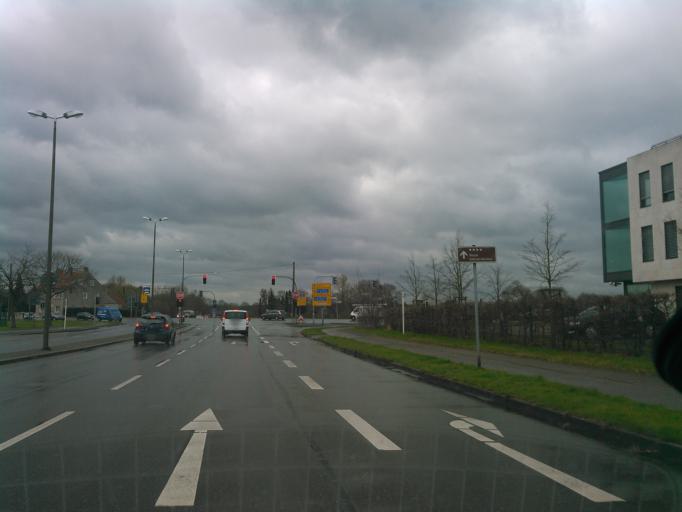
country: DE
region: North Rhine-Westphalia
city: Marl
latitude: 51.6412
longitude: 7.1005
